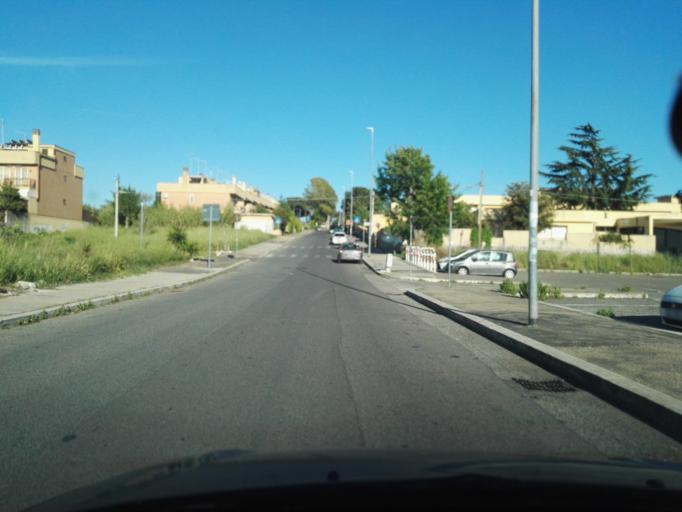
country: IT
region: Latium
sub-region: Citta metropolitana di Roma Capitale
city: Selcetta
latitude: 41.7694
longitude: 12.4741
